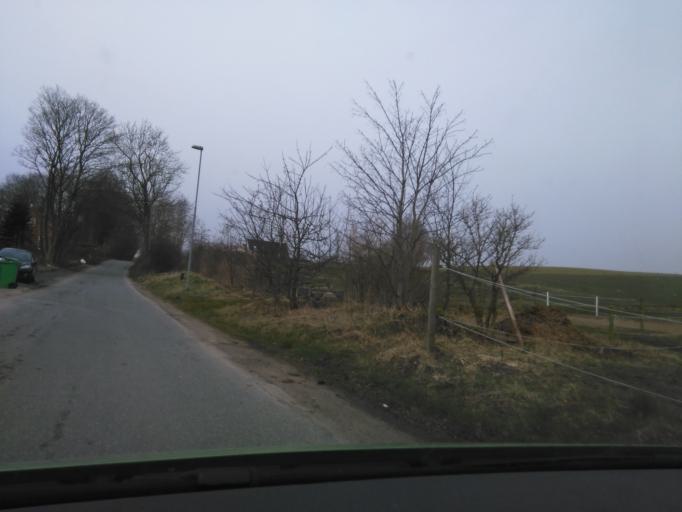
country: DK
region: Central Jutland
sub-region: Arhus Kommune
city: Marslet
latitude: 56.0829
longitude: 10.1755
